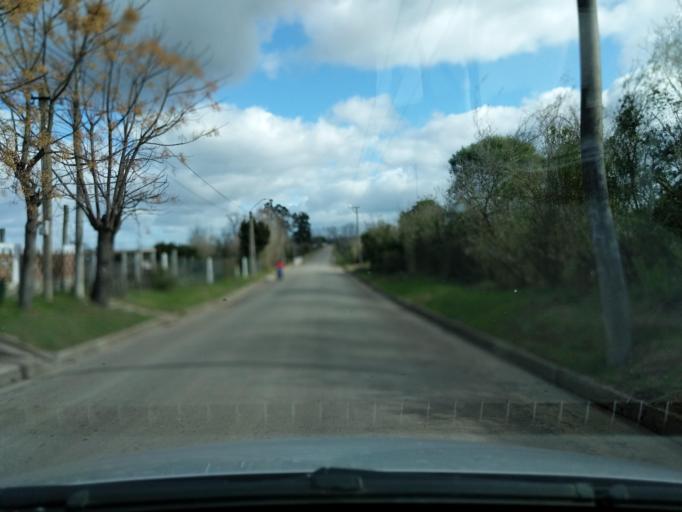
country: UY
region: Florida
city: Florida
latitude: -34.1072
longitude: -56.2182
